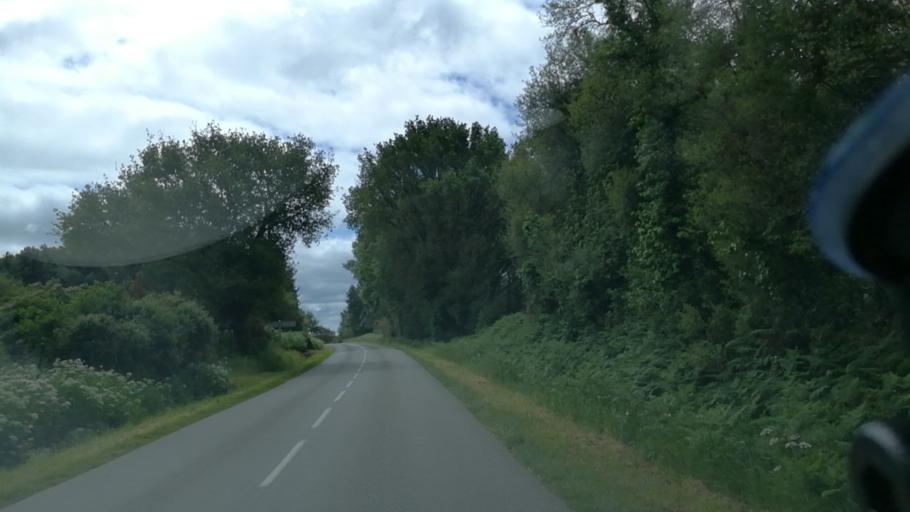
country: FR
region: Brittany
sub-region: Departement du Morbihan
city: Penestin
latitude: 47.4736
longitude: -2.4330
